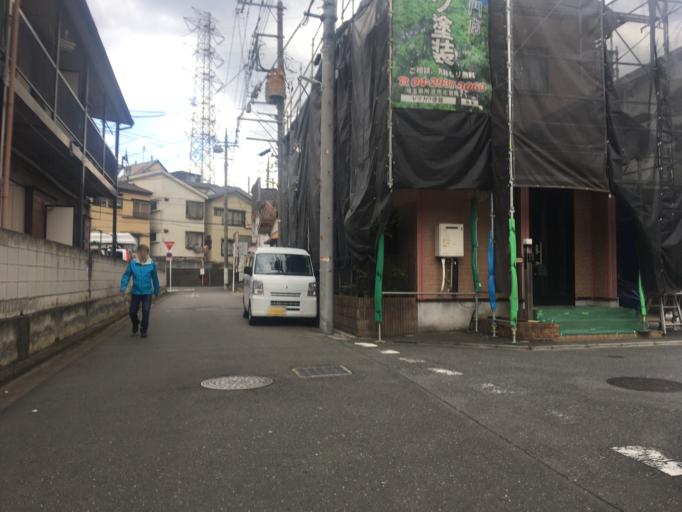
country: JP
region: Saitama
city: Shiki
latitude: 35.8191
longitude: 139.5587
